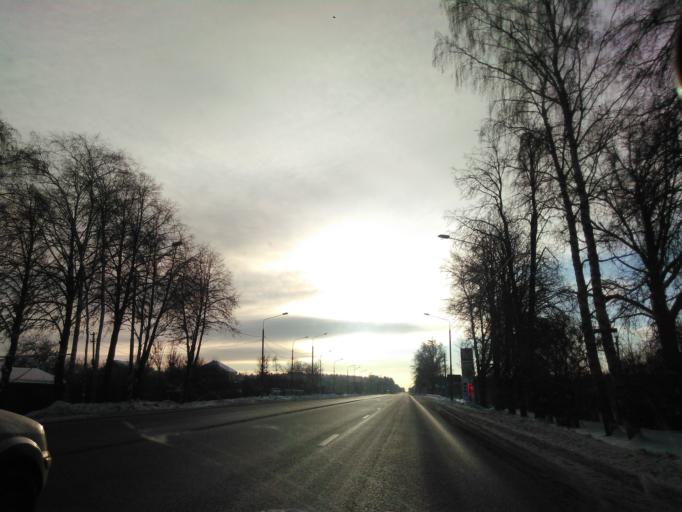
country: RU
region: Moskovskaya
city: Reshetnikovo
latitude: 56.4666
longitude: 36.5857
